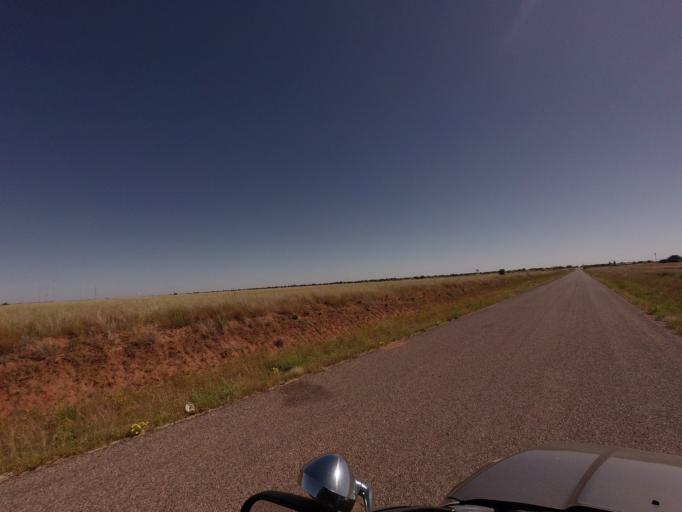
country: US
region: New Mexico
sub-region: Curry County
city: Clovis
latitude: 34.4408
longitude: -103.2317
